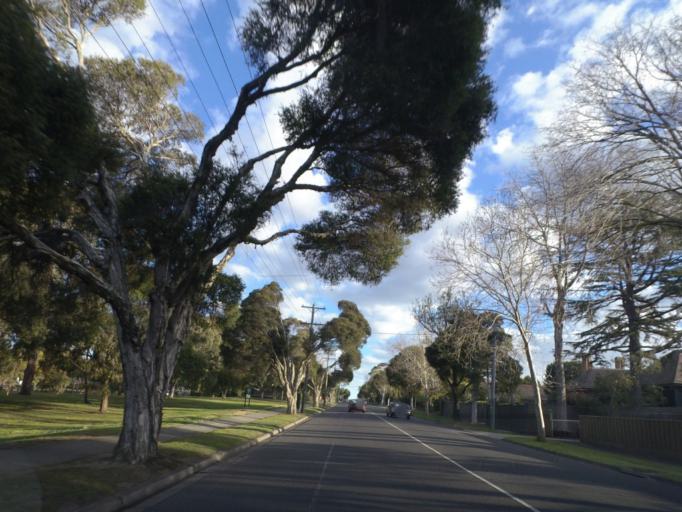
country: AU
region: Victoria
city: Mont Albert
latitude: -37.8112
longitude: 145.1002
